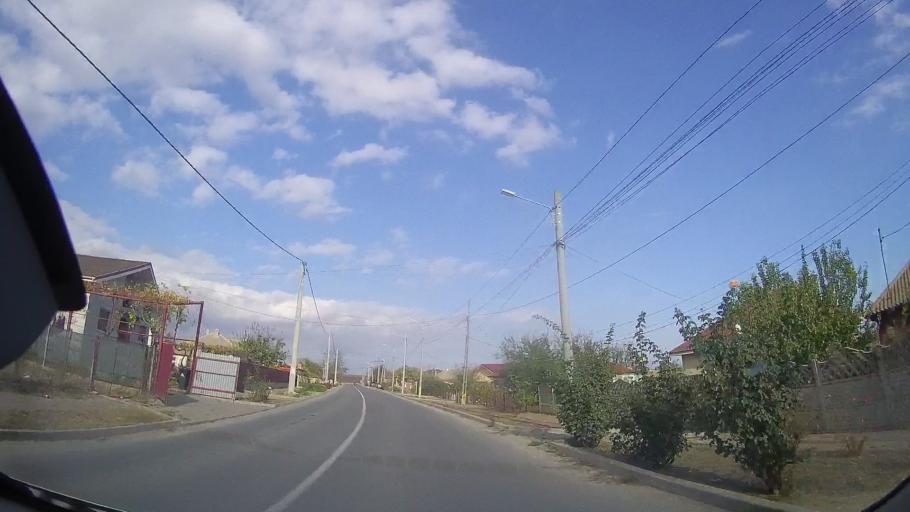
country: RO
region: Constanta
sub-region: Comuna Douazeci si Trei August
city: Dulcesti
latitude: 43.9084
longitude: 28.5491
